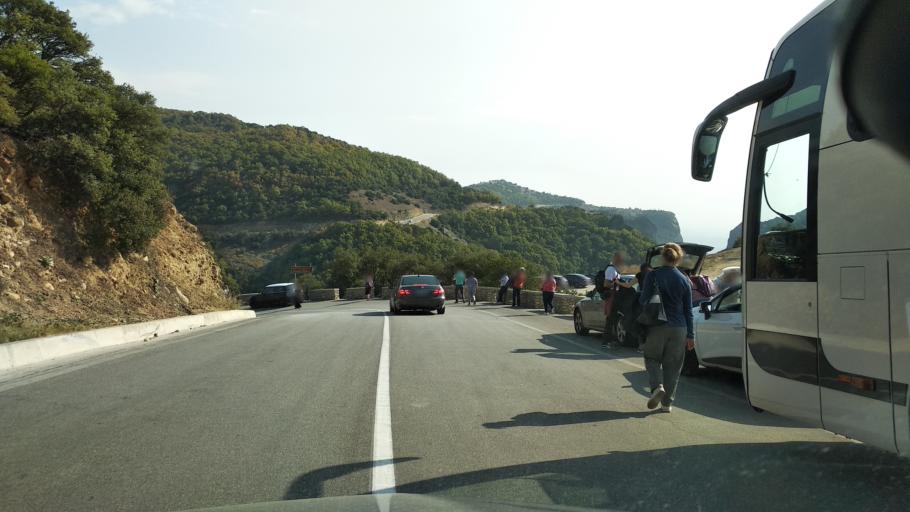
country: GR
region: Thessaly
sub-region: Trikala
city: Kastraki
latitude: 39.7264
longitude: 21.6322
